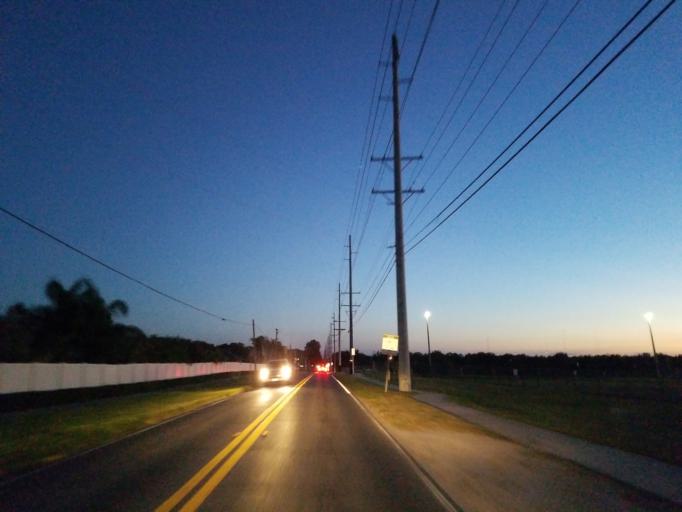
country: US
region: Florida
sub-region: Hillsborough County
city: Bloomingdale
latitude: 27.9074
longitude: -82.2278
